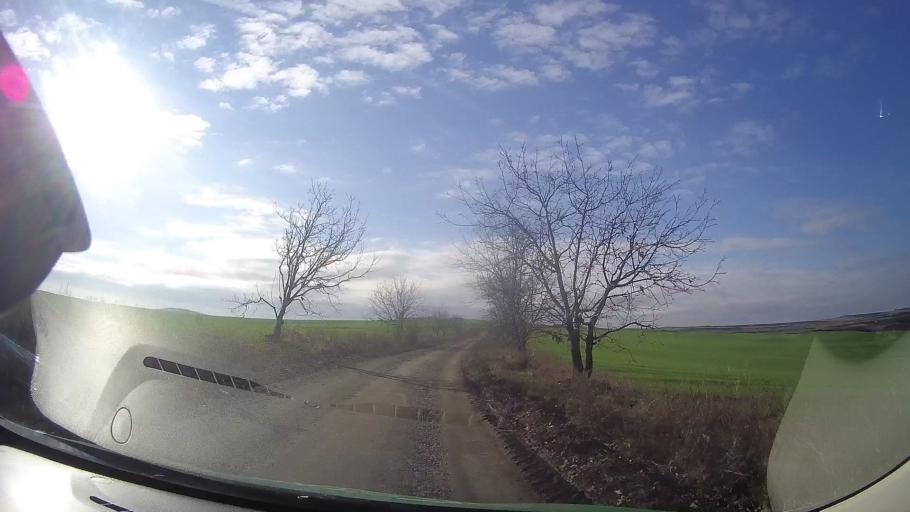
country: RO
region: Mures
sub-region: Comuna Saulia
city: Saulia
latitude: 46.6039
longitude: 24.2422
